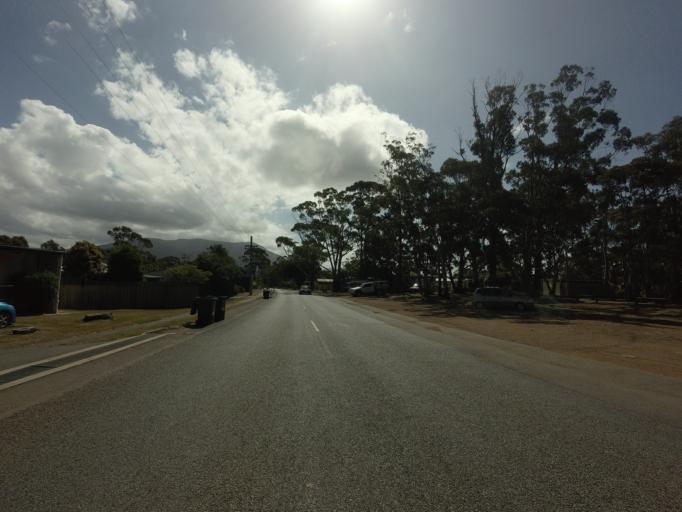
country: AU
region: Tasmania
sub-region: Hobart
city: Dynnyrne
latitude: -42.9248
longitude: 147.3288
